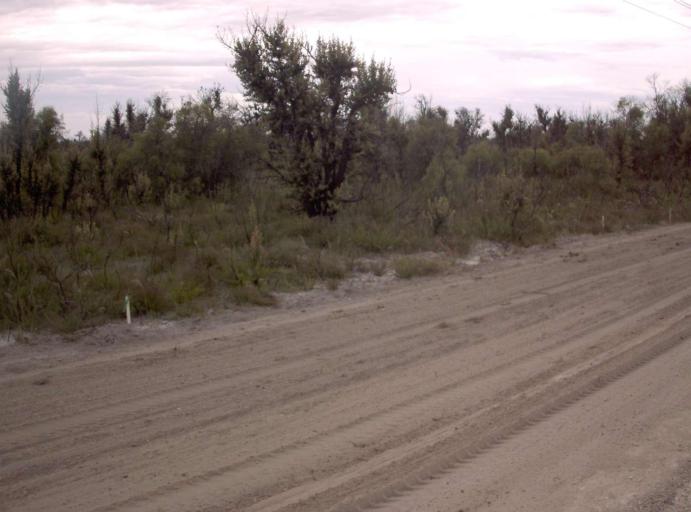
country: AU
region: Victoria
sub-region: East Gippsland
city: Bairnsdale
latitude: -38.1065
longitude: 147.4788
